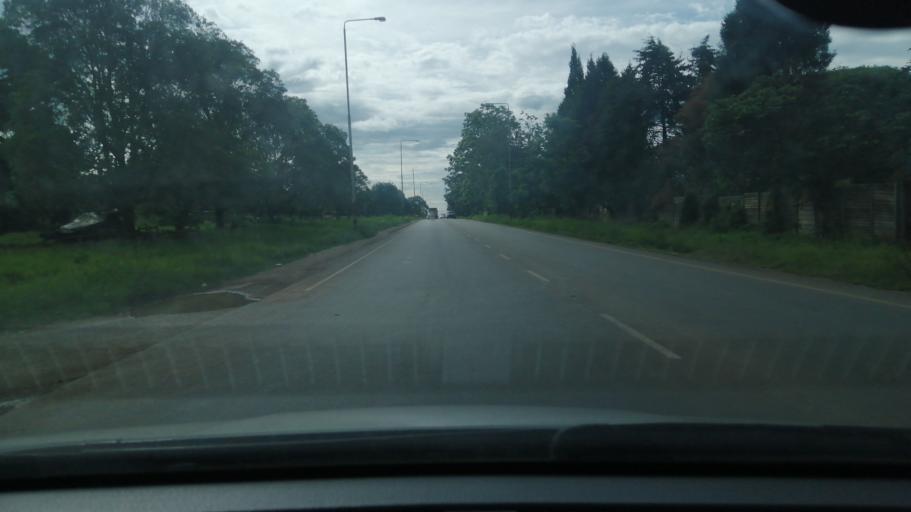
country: ZW
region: Harare
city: Harare
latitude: -17.7631
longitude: 30.9866
